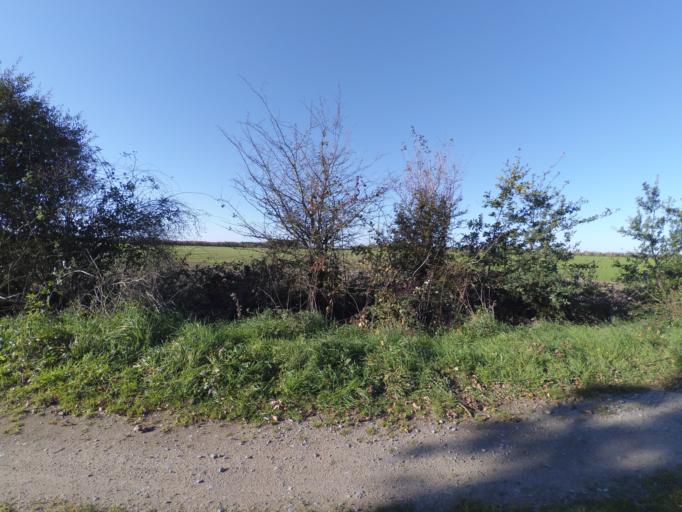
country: FR
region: Pays de la Loire
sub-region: Departement de la Loire-Atlantique
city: La Planche
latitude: 47.0277
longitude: -1.3984
